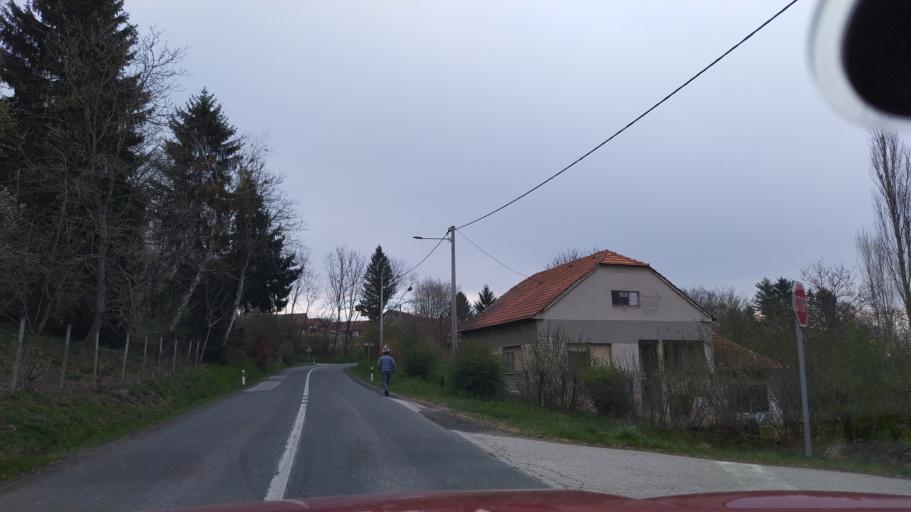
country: HR
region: Varazdinska
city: Ludbreg
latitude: 46.2301
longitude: 16.5459
